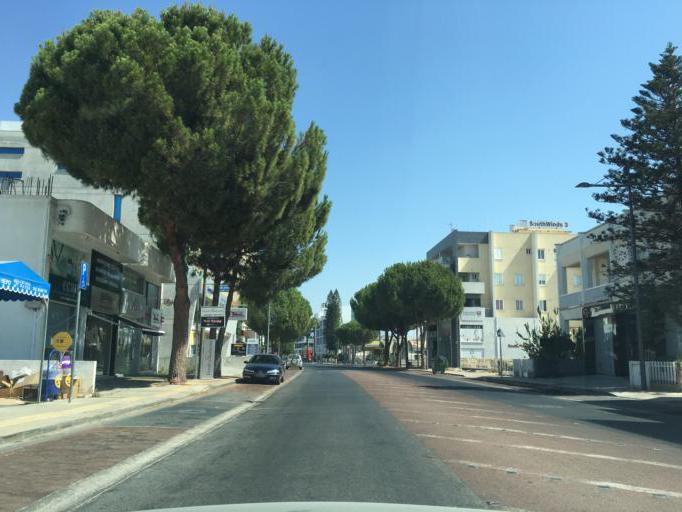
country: CY
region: Lefkosia
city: Nicosia
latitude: 35.1604
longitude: 33.3170
